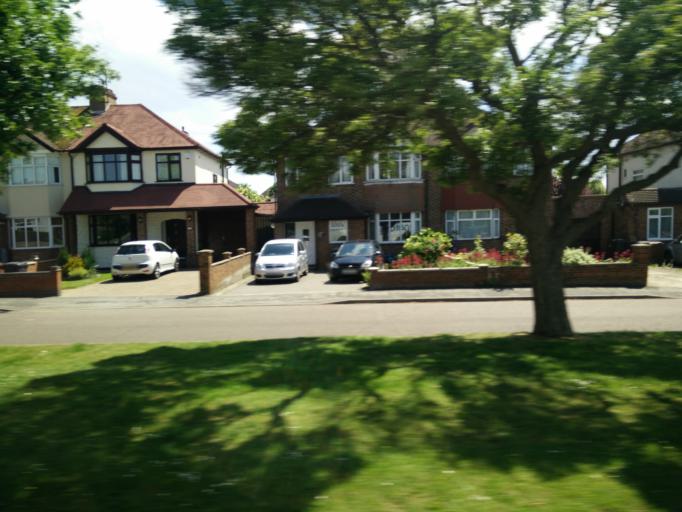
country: GB
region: England
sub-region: Hertfordshire
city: Letchworth
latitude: 51.9586
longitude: -0.2526
